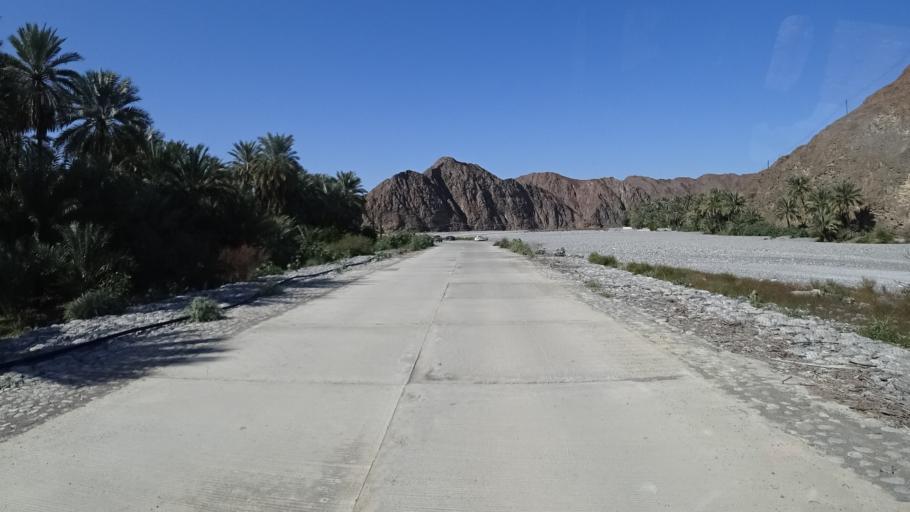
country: OM
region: Al Batinah
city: Bayt al `Awabi
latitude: 23.3840
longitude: 57.6617
